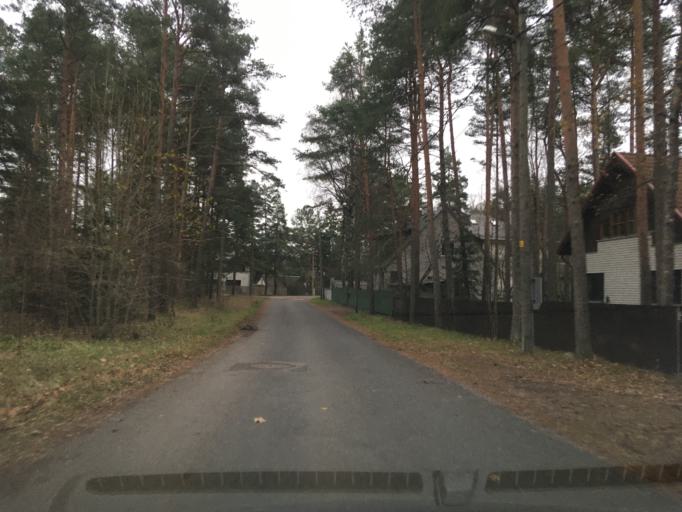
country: EE
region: Harju
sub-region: Saku vald
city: Saku
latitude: 59.3730
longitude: 24.6991
